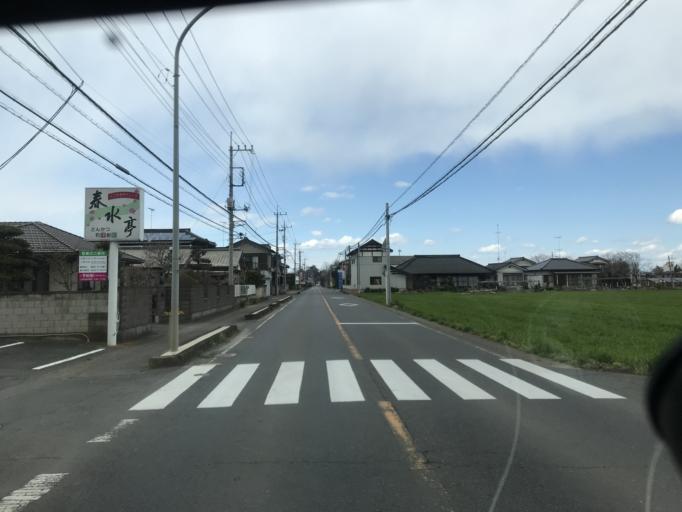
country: JP
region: Ibaraki
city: Shimodate
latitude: 36.2407
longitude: 139.9771
